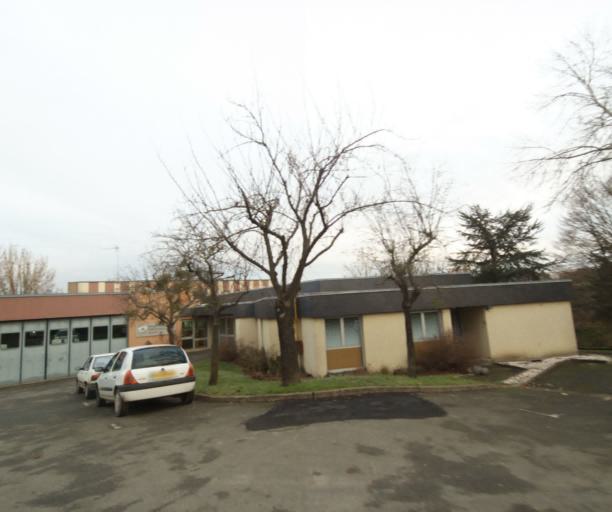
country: FR
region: Pays de la Loire
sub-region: Departement de la Sarthe
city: Coulaines
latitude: 48.0157
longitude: 0.2062
